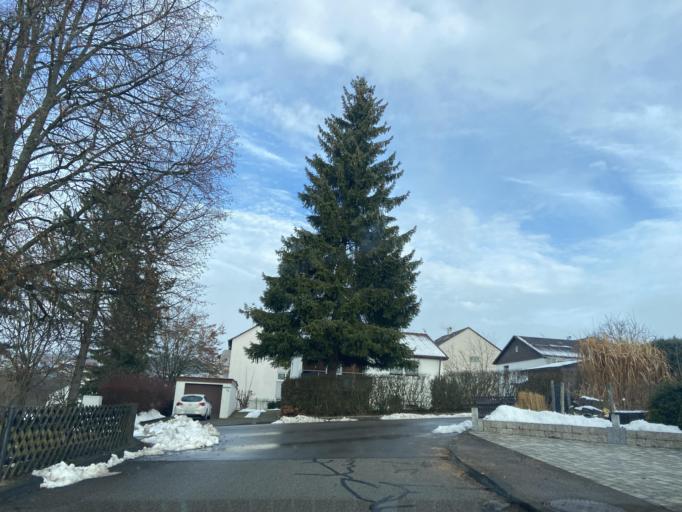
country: DE
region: Baden-Wuerttemberg
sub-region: Tuebingen Region
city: Gammertingen
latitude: 48.2529
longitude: 9.2242
